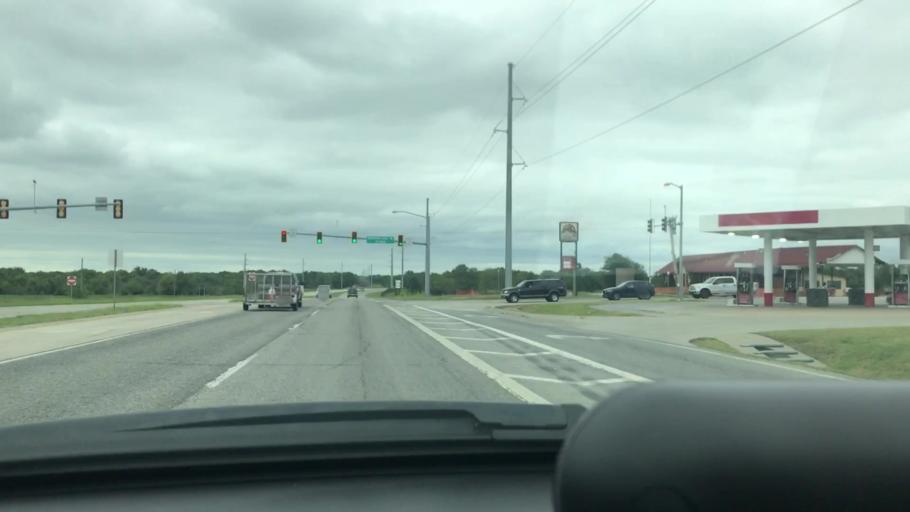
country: US
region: Oklahoma
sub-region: Wagoner County
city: Wagoner
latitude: 36.0163
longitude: -95.3684
